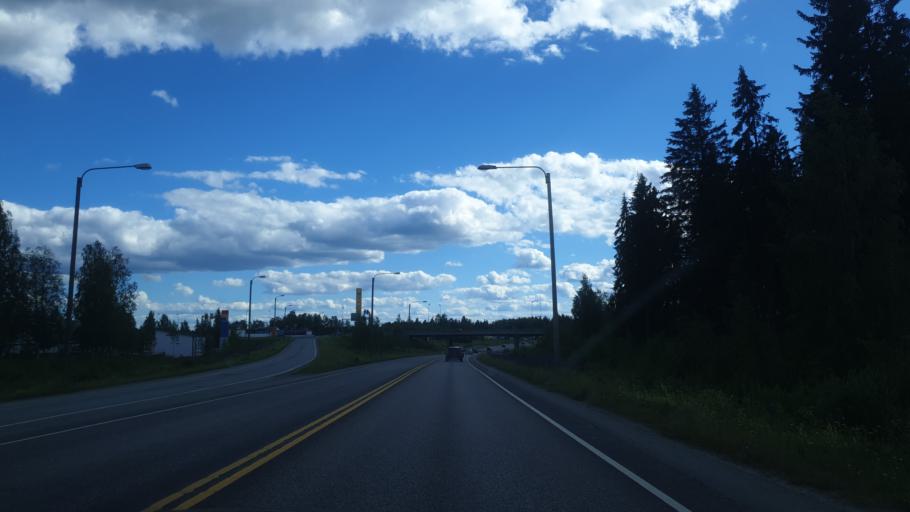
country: FI
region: Southern Savonia
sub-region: Pieksaemaeki
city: Juva
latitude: 61.9010
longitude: 27.8039
